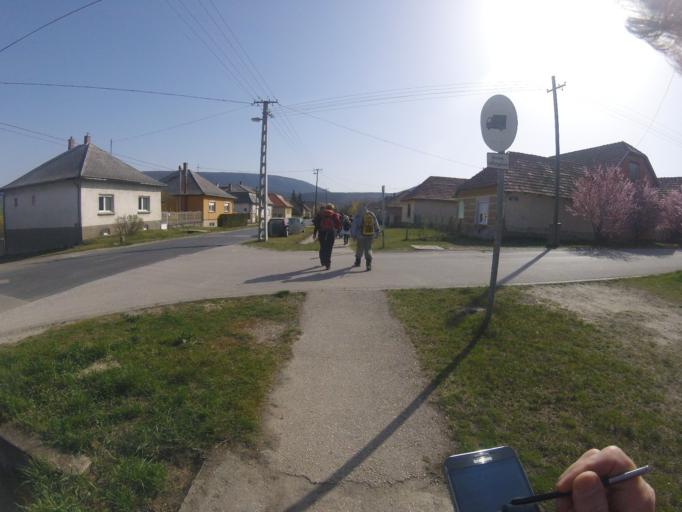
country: HU
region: Komarom-Esztergom
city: Piliscsev
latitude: 47.6727
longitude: 18.8124
